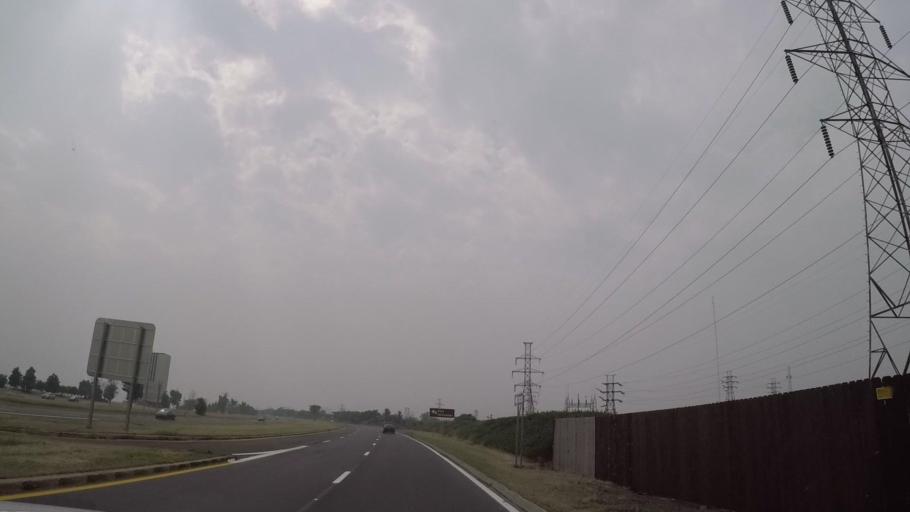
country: US
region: New York
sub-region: Niagara County
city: Niagara Falls
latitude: 43.0778
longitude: -79.0133
